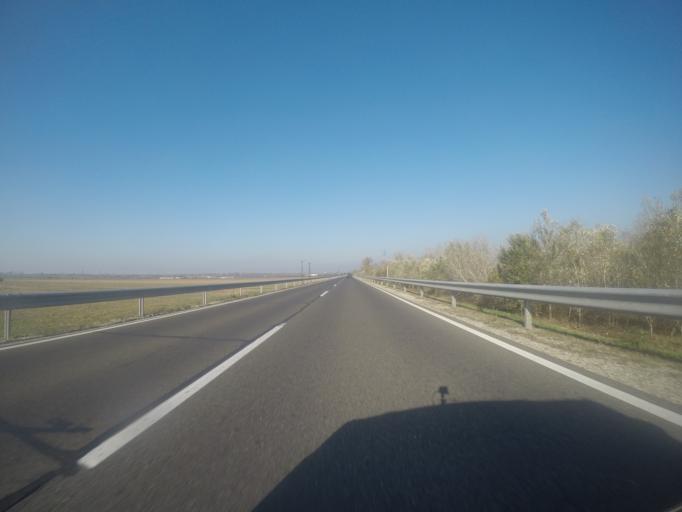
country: HU
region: Fejer
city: Ercsi
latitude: 47.2208
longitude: 18.8882
